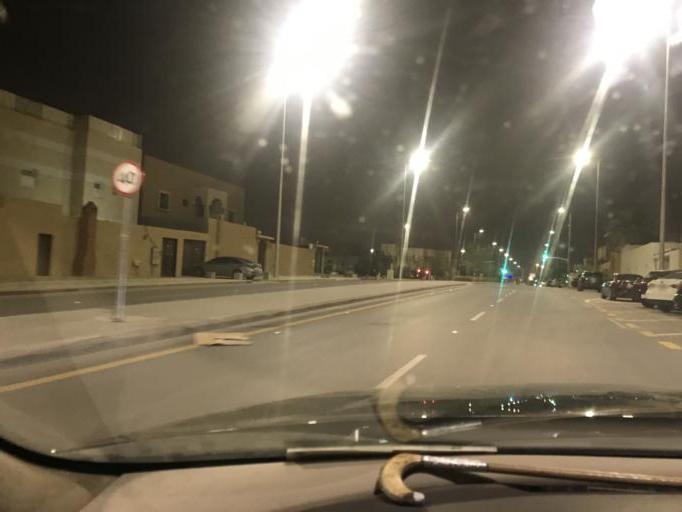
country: SA
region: Ar Riyad
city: Riyadh
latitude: 24.7260
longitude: 46.7898
